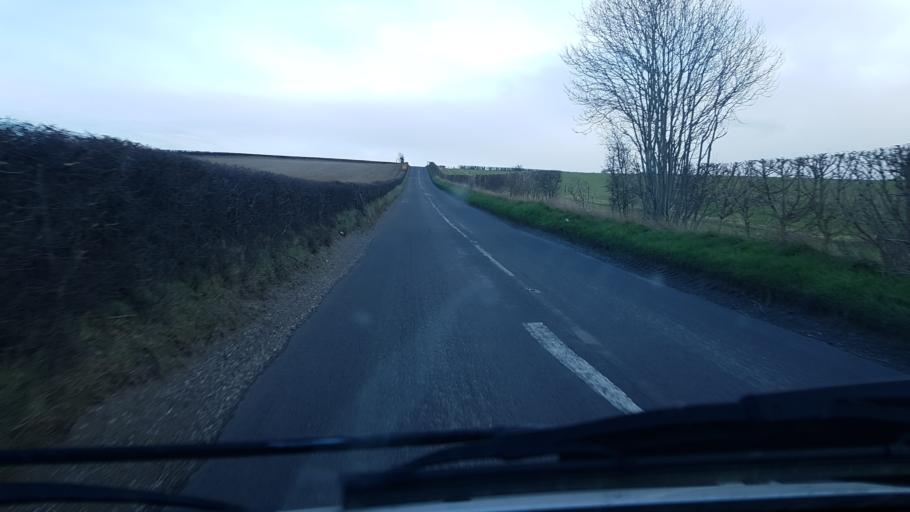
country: GB
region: England
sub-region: Wiltshire
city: Collingbourne Kingston
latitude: 51.2703
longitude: -1.6471
